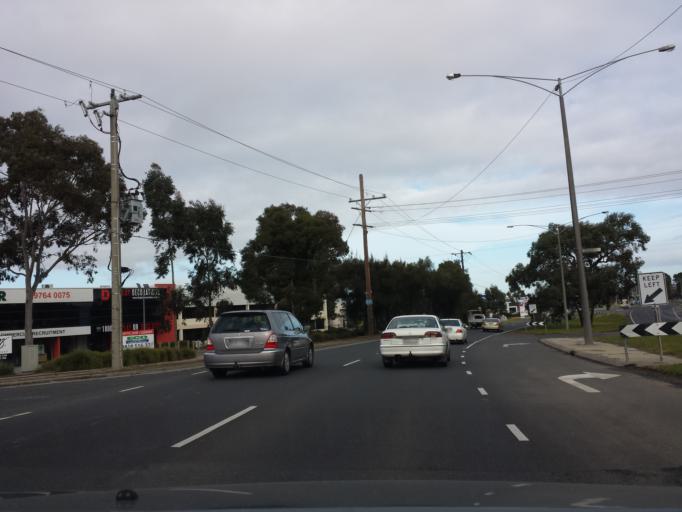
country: AU
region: Victoria
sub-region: Knox
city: Knoxfield
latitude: -37.8972
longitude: 145.2461
